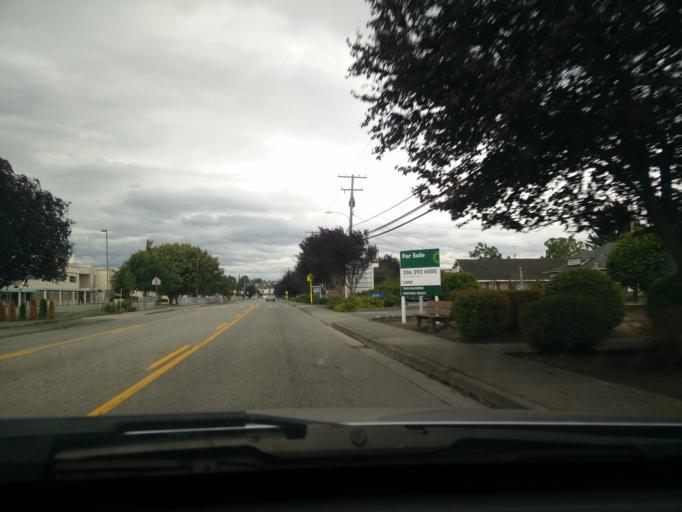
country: US
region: Washington
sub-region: Snohomish County
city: Stanwood
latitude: 48.2421
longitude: -122.3632
